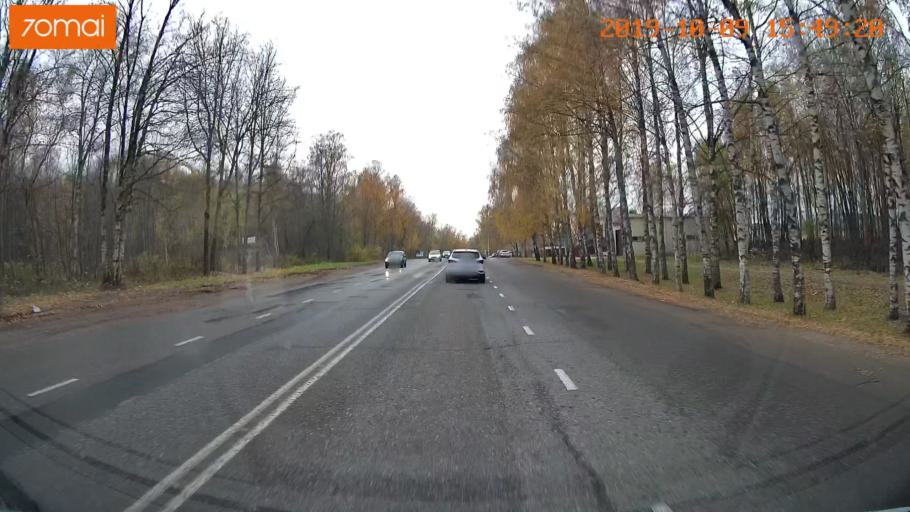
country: RU
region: Kostroma
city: Oktyabr'skiy
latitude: 57.8057
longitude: 41.0059
